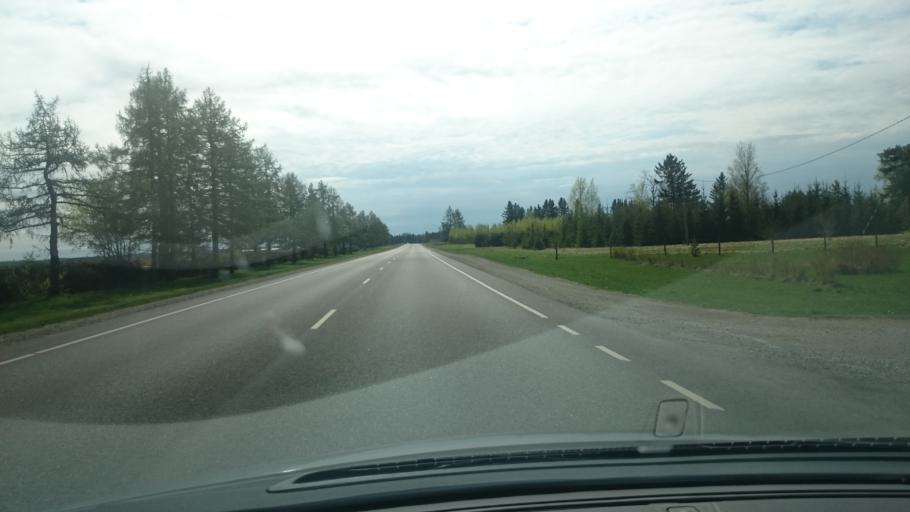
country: EE
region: Laeaene-Virumaa
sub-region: Rakvere linn
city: Rakvere
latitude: 59.4080
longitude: 26.3620
